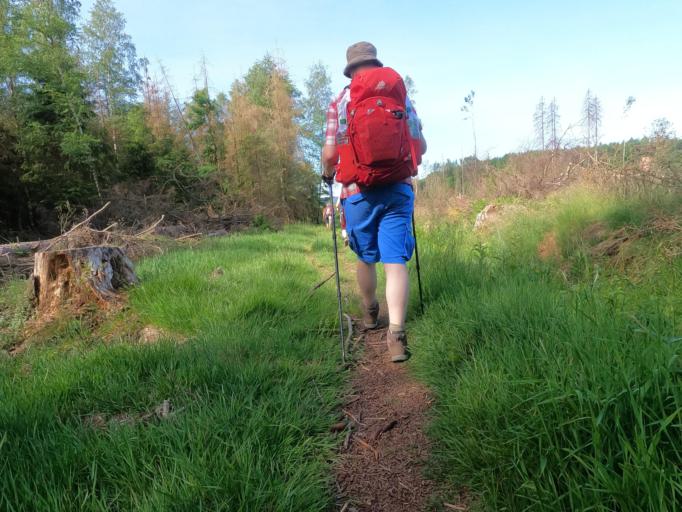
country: DE
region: Rheinland-Pfalz
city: Bolsberg
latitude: 50.6601
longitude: 7.9228
